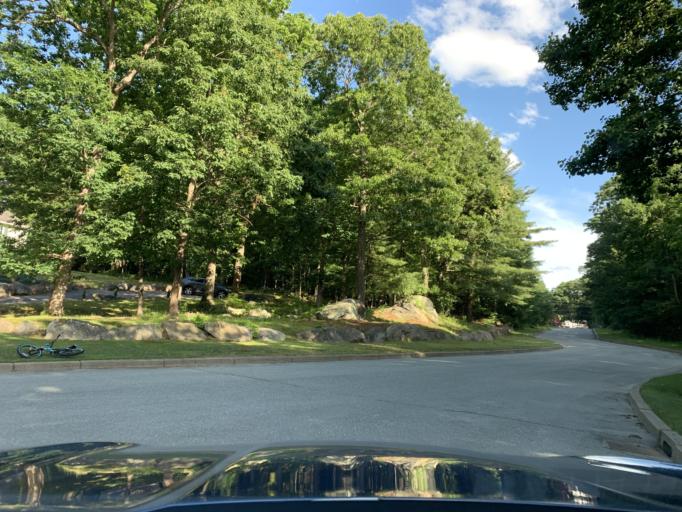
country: US
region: Rhode Island
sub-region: Kent County
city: West Warwick
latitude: 41.6604
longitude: -71.5240
